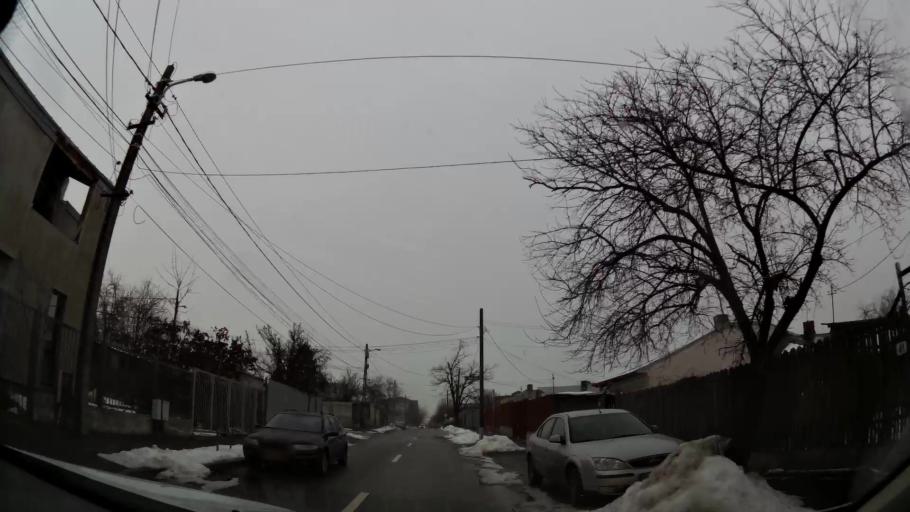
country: RO
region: Ilfov
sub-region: Comuna Mogosoaia
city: Mogosoaia
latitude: 44.5086
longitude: 26.0181
